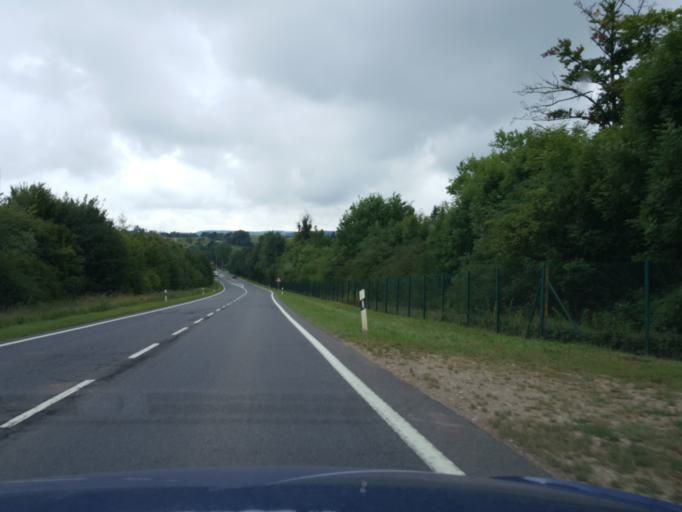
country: LU
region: Luxembourg
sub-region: Canton de Mersch
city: Bissen
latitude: 49.7696
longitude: 6.0867
